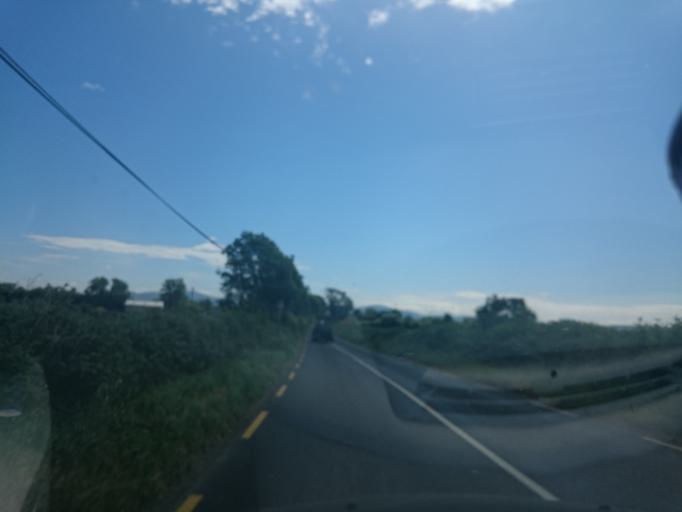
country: IE
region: Leinster
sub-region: Kilkenny
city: Thomastown
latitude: 52.6396
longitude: -7.1028
